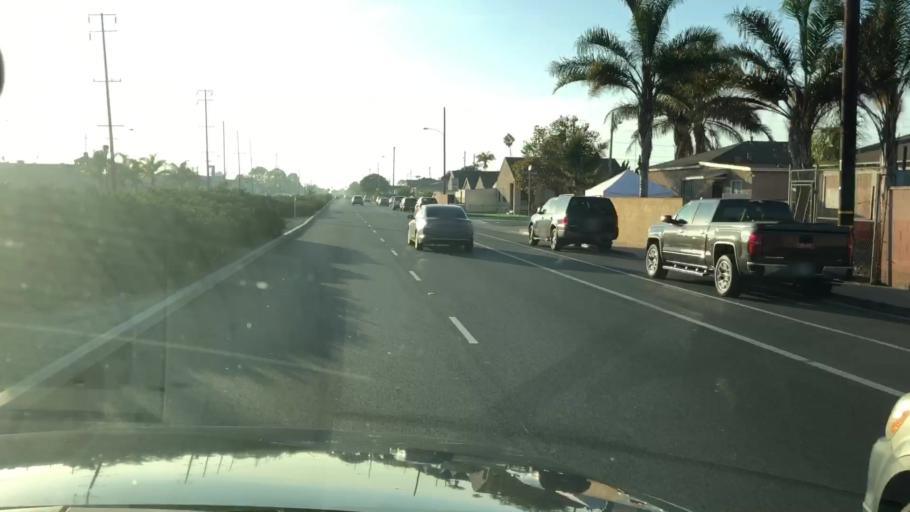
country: US
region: California
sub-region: Ventura County
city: Oxnard
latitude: 34.1899
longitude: -119.1843
